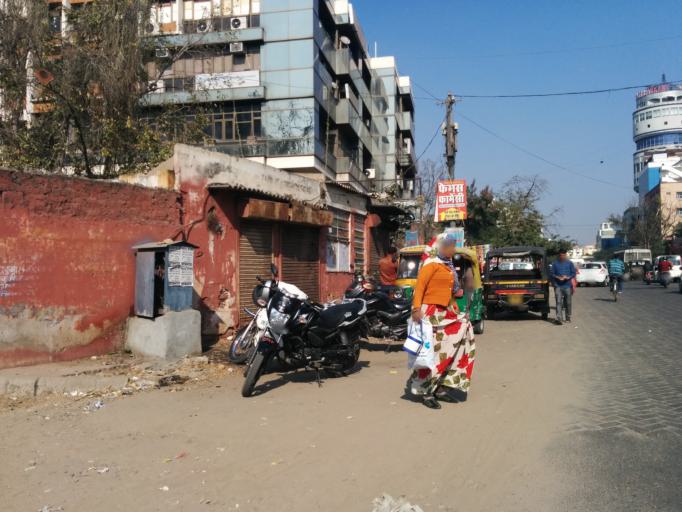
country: IN
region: Rajasthan
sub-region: Jaipur
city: Jaipur
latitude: 26.9163
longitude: 75.7988
